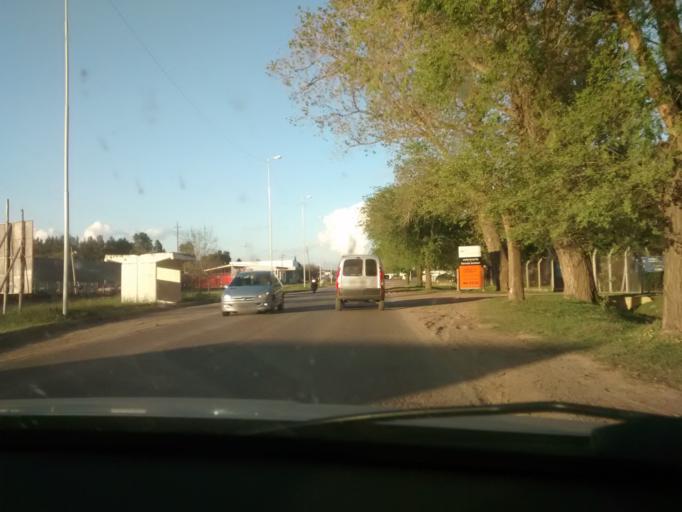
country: AR
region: Buenos Aires
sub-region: Partido de Brandsen
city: Brandsen
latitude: -35.1651
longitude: -58.2228
